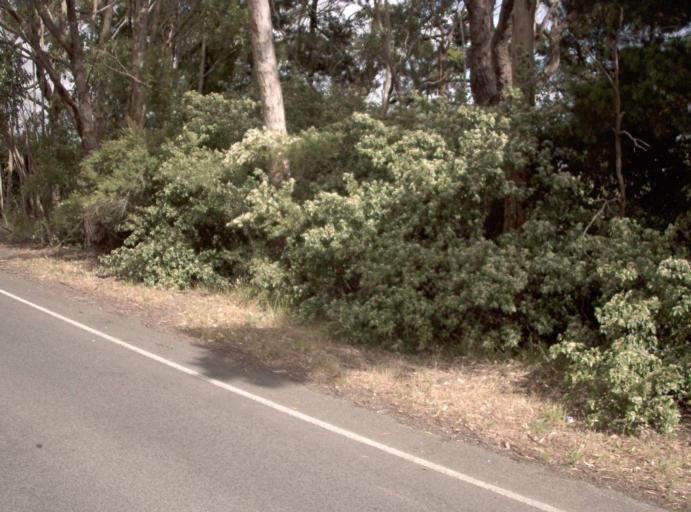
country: AU
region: Victoria
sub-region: Latrobe
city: Morwell
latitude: -38.1864
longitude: 146.4560
